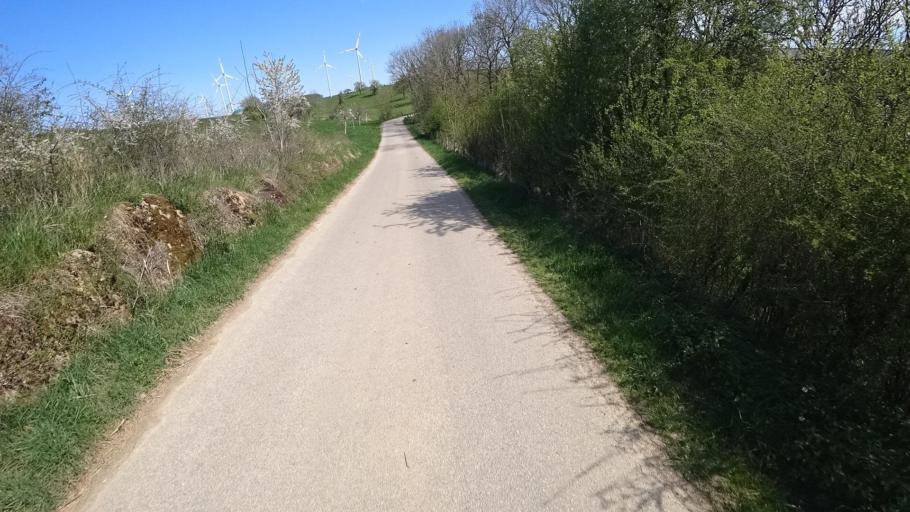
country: DE
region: Rheinland-Pfalz
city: Eisenach
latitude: 49.8488
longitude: 6.5135
